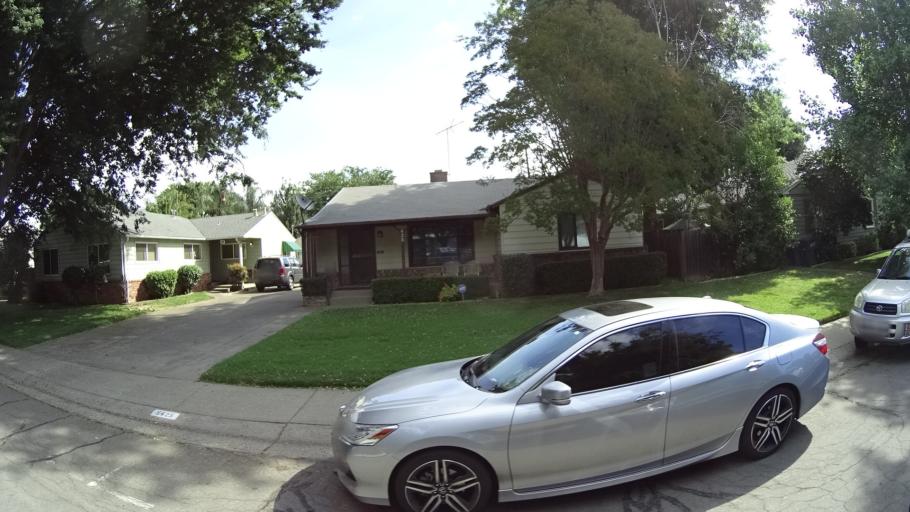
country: US
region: California
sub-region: Sacramento County
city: Arden-Arcade
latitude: 38.5768
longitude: -121.4295
